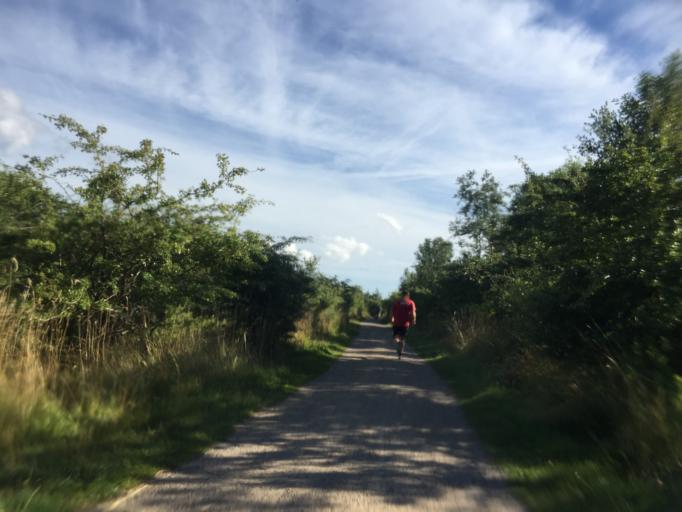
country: DK
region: Capital Region
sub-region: Kobenhavn
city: Christianshavn
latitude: 55.6507
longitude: 12.5827
